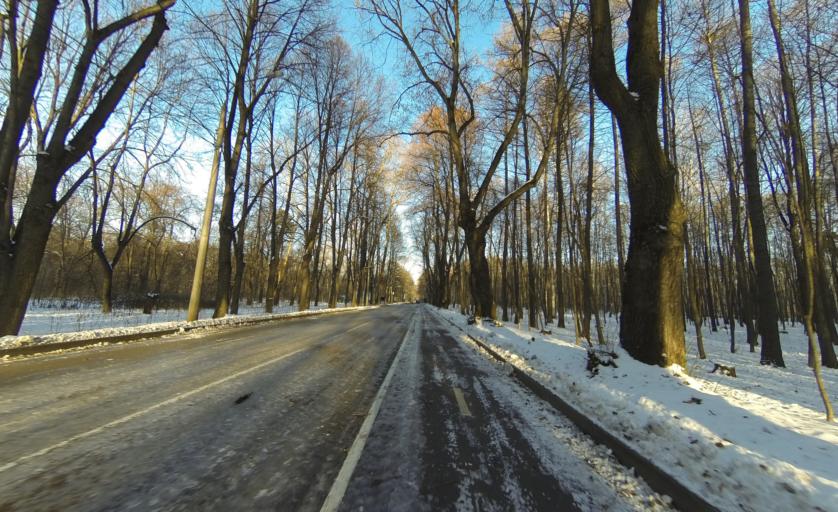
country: RU
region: Moscow
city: Sokol'niki
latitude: 55.8062
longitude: 37.6812
